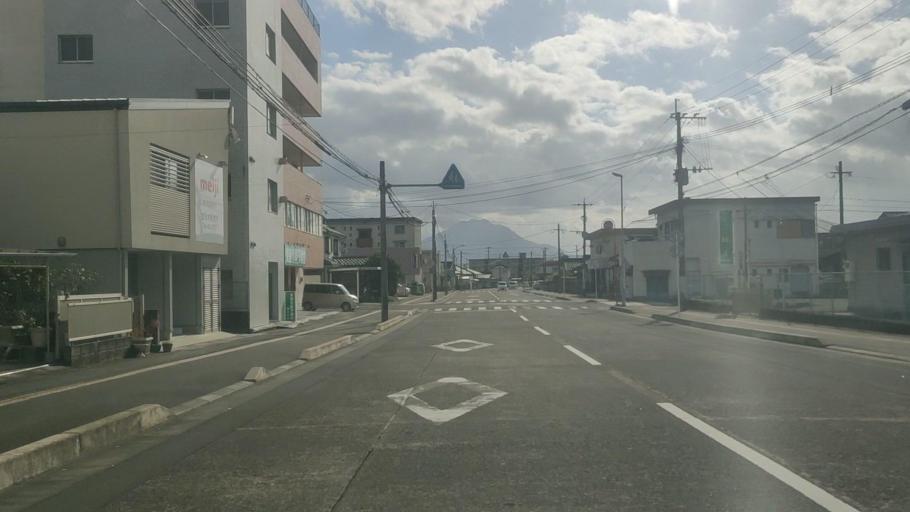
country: JP
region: Kagoshima
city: Kajiki
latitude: 31.7370
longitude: 130.6702
